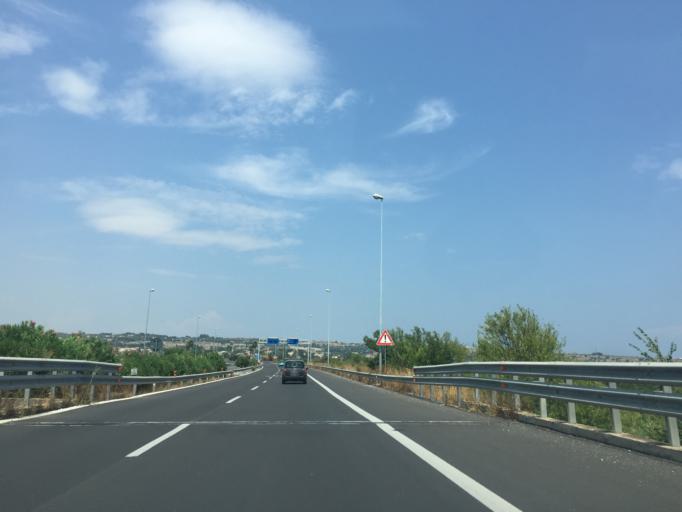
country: IT
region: Sicily
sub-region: Provincia di Siracusa
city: Belvedere
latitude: 37.0668
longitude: 15.2260
